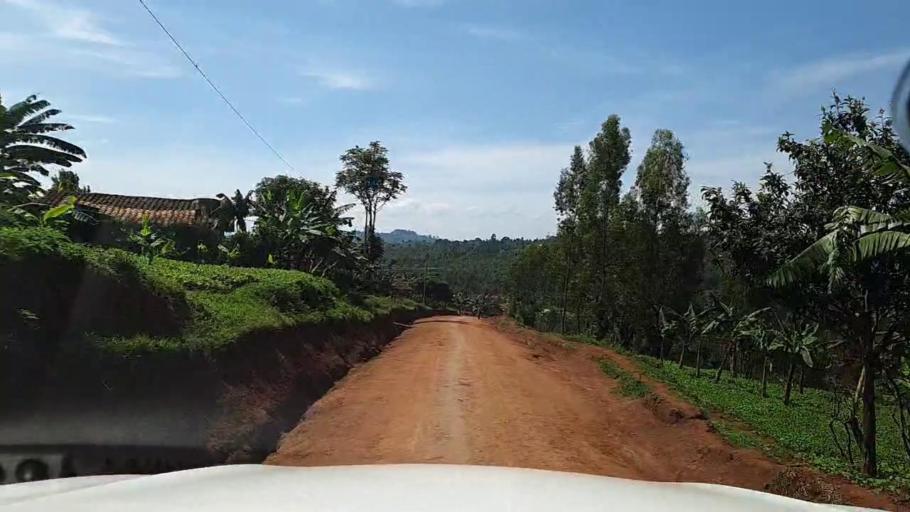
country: RW
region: Southern Province
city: Butare
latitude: -2.6972
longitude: 29.8546
